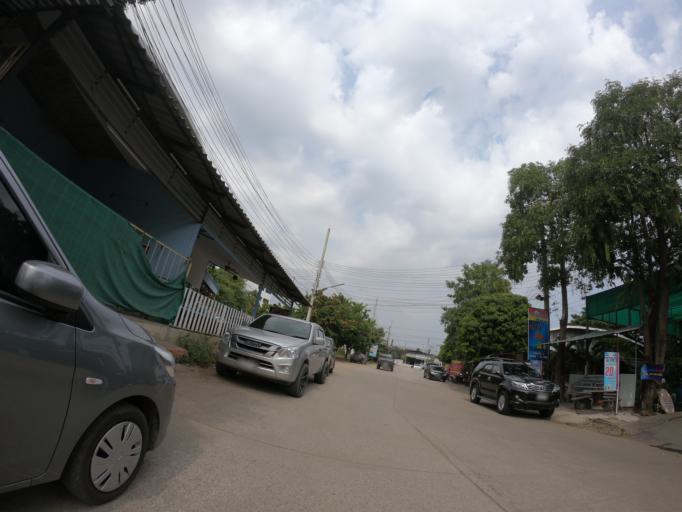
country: TH
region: Chiang Mai
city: Chiang Mai
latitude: 18.7668
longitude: 98.9830
